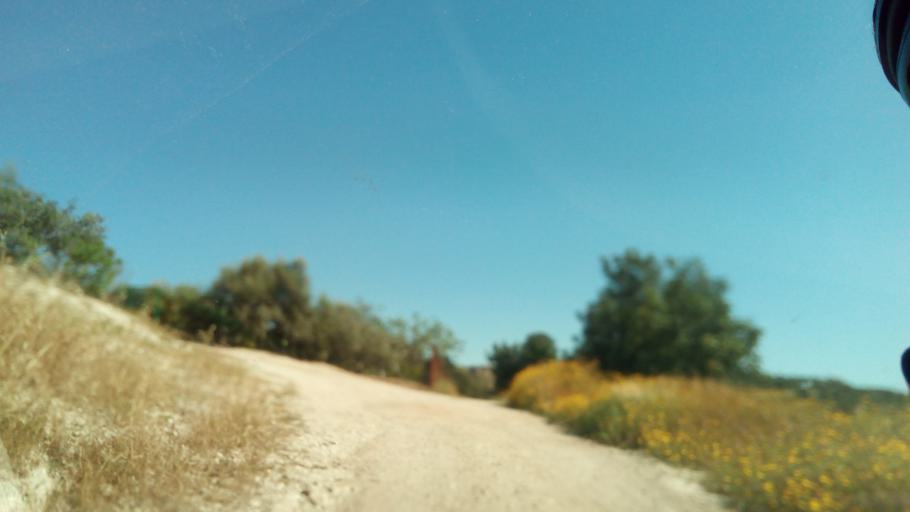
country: CY
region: Limassol
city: Pissouri
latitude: 34.6737
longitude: 32.6871
